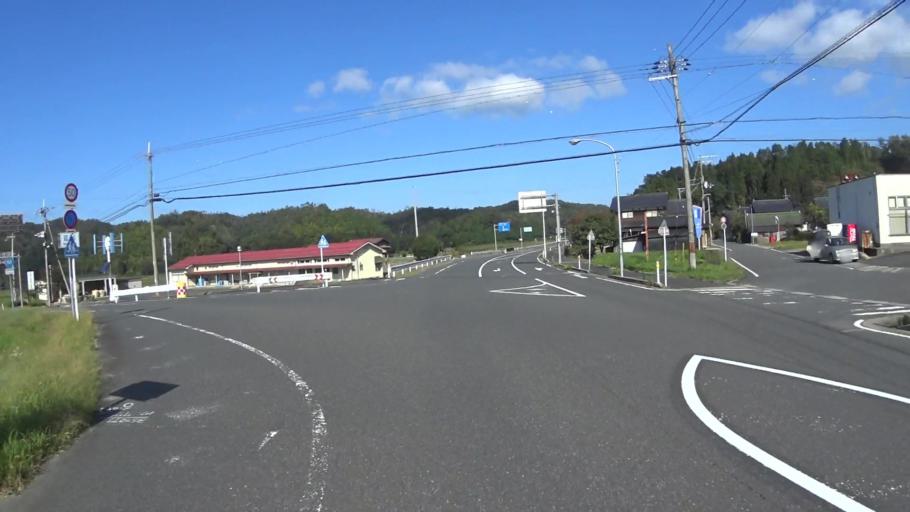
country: JP
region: Kyoto
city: Miyazu
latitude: 35.5969
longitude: 135.1409
